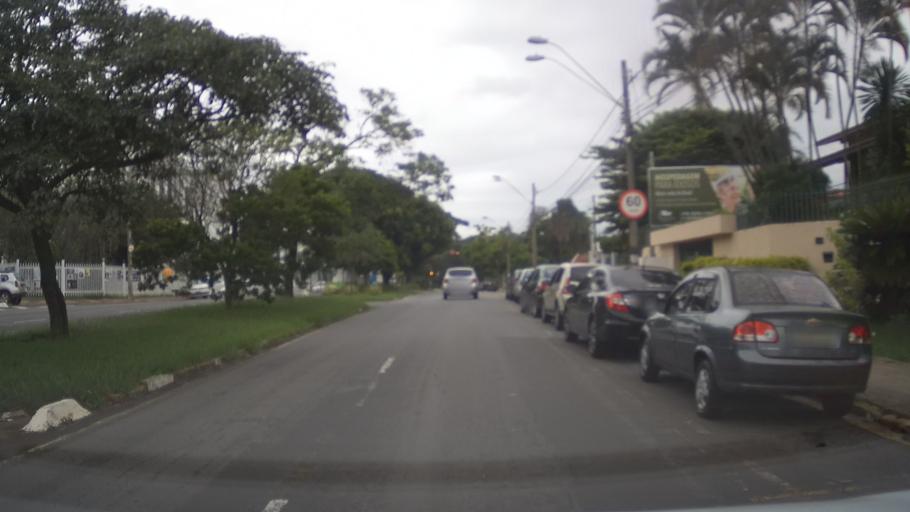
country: BR
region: Sao Paulo
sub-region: Campinas
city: Campinas
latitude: -22.8997
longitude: -47.0431
